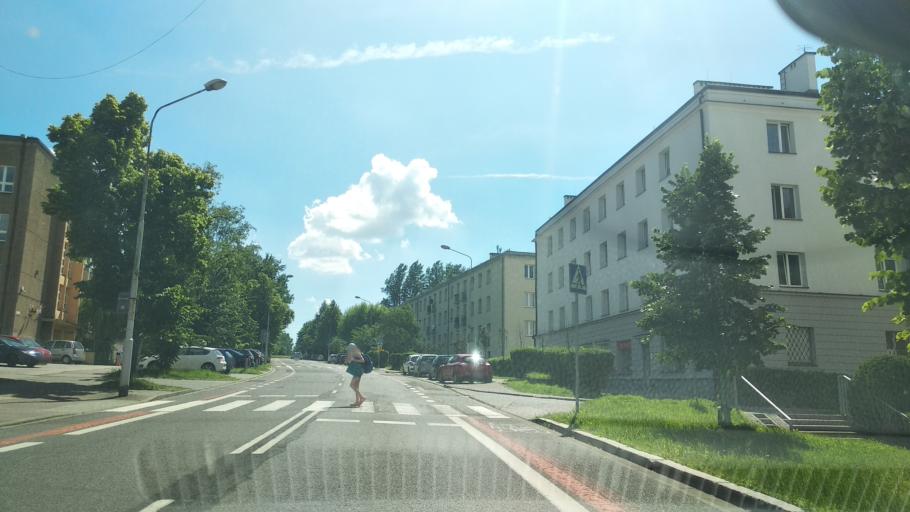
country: PL
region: Silesian Voivodeship
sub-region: Katowice
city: Katowice
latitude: 50.2527
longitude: 19.0021
